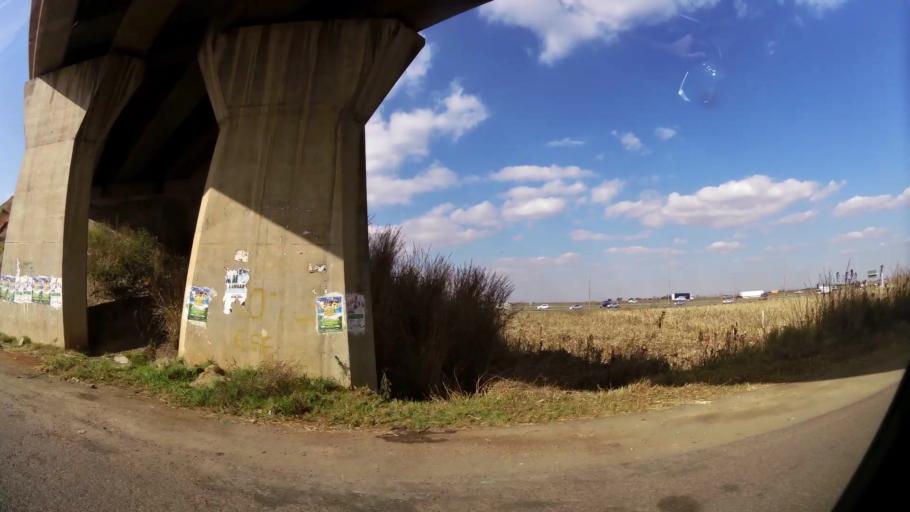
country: ZA
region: Gauteng
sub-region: Ekurhuleni Metropolitan Municipality
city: Tembisa
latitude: -25.9901
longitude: 28.2494
